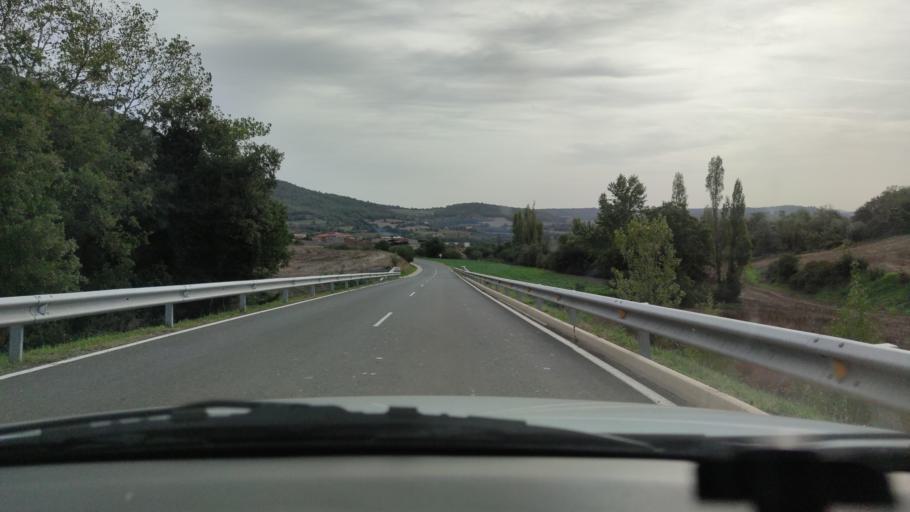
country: ES
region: Catalonia
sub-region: Provincia de Lleida
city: Artesa de Segre
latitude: 41.9934
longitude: 1.0138
